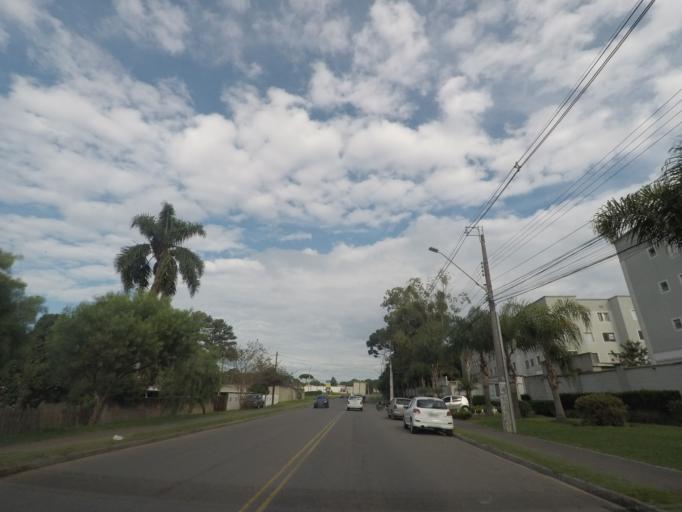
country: BR
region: Parana
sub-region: Sao Jose Dos Pinhais
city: Sao Jose dos Pinhais
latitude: -25.5565
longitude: -49.2926
